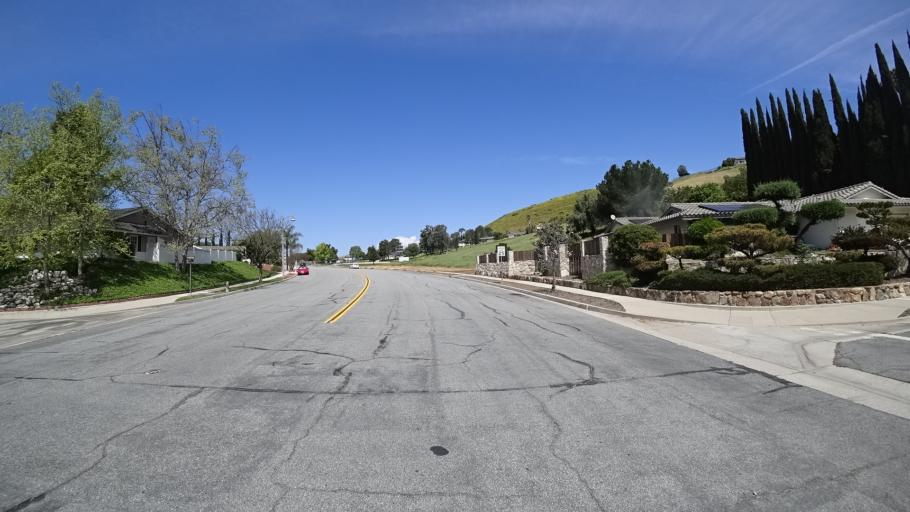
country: US
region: California
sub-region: Ventura County
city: Moorpark
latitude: 34.2390
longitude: -118.8483
